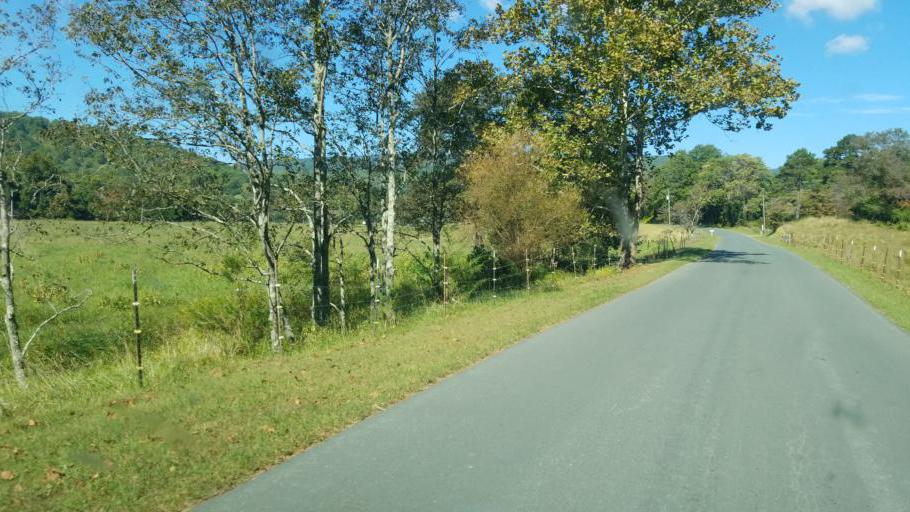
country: US
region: Virginia
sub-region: Greene County
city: Stanardsville
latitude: 38.3628
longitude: -78.4202
